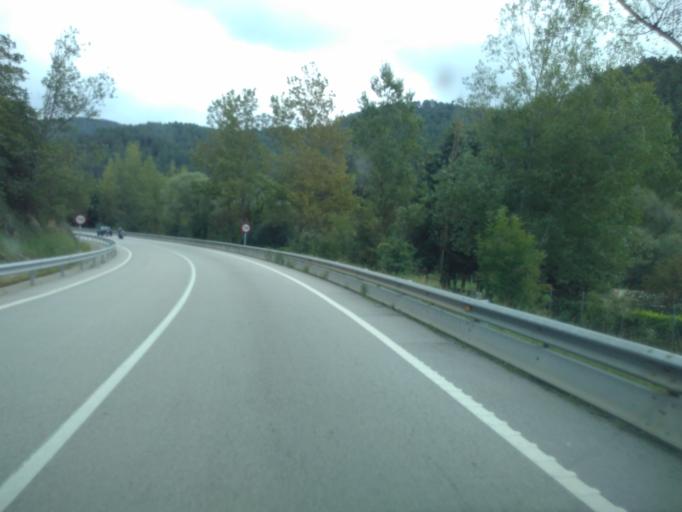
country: ES
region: Catalonia
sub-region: Provincia de Girona
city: Ripoll
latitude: 42.1659
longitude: 2.1997
